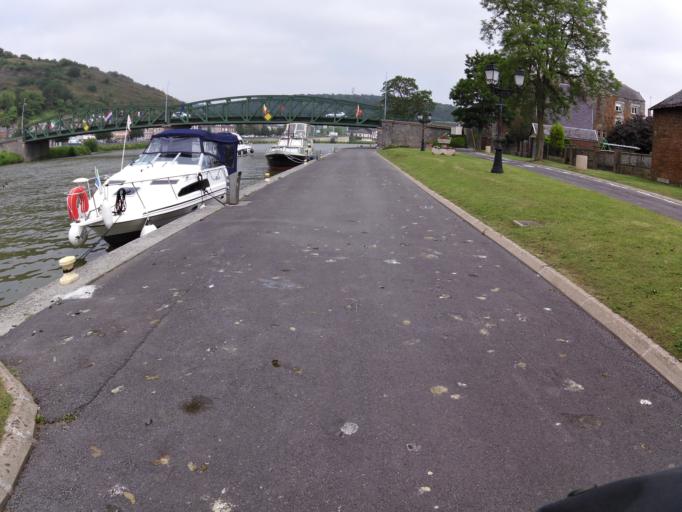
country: FR
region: Champagne-Ardenne
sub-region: Departement des Ardennes
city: Vireux-Wallerand
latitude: 50.0843
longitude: 4.7265
